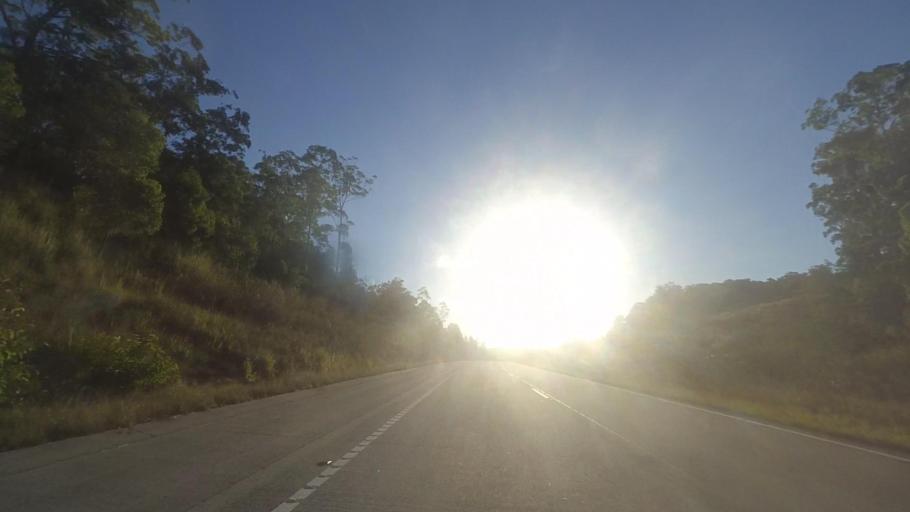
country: AU
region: New South Wales
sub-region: Great Lakes
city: Hawks Nest
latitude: -32.5355
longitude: 152.1779
